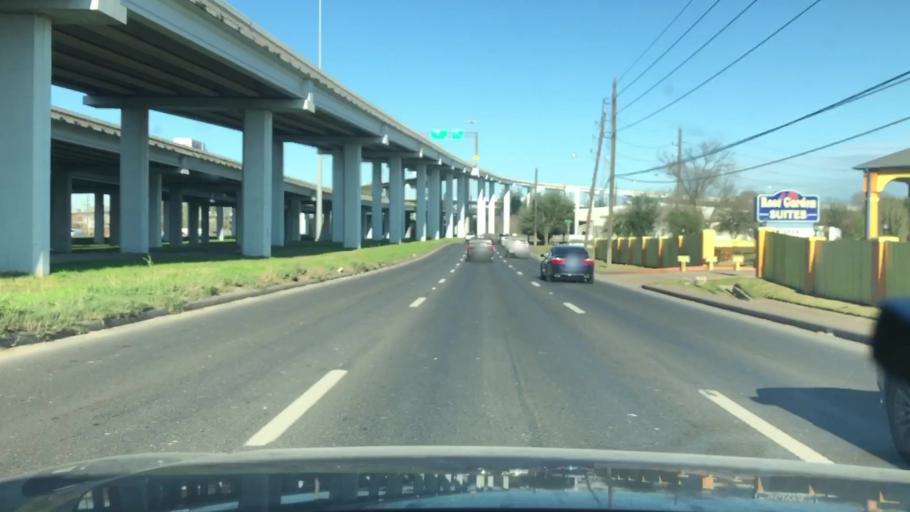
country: US
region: Texas
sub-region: Fort Bend County
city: Meadows Place
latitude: 29.6569
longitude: -95.5534
